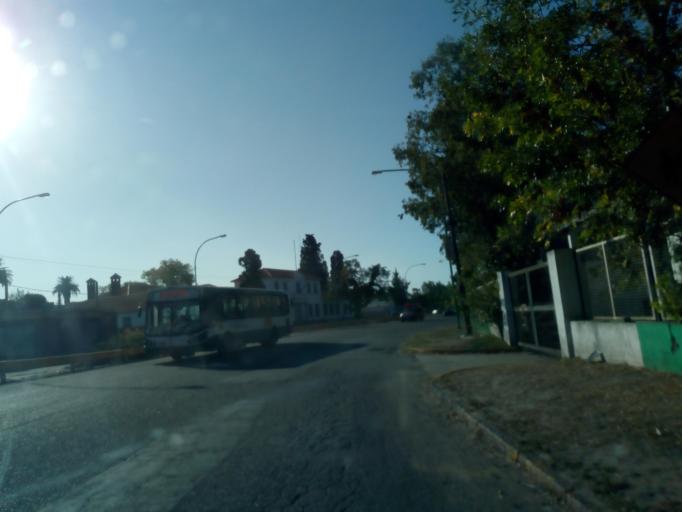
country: AR
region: Buenos Aires
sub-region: Partido de Ensenada
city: Ensenada
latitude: -34.8152
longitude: -57.9769
